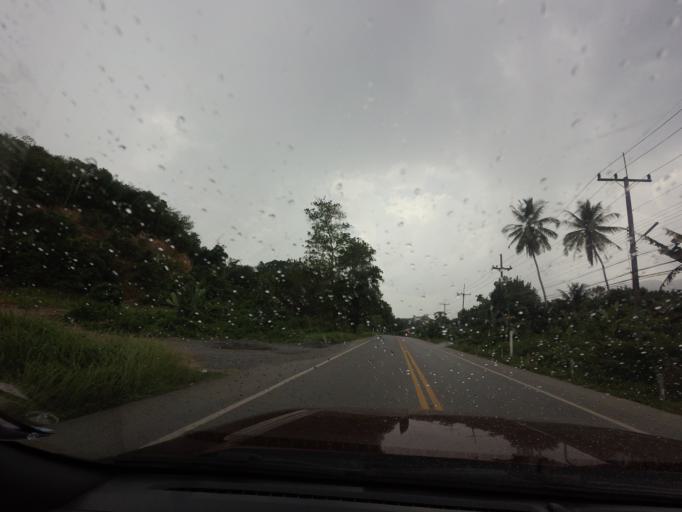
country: TH
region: Yala
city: Krong Pi Nang
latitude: 6.3683
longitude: 101.2993
